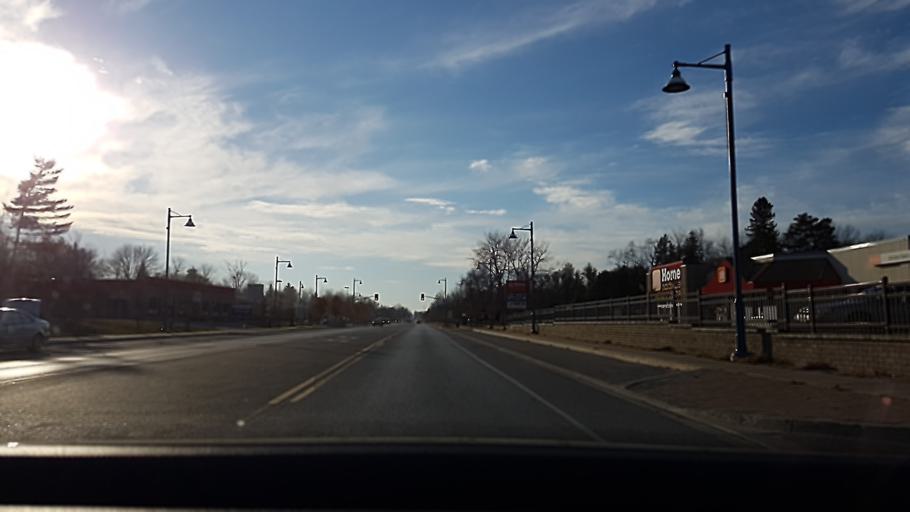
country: CA
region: Ontario
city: Keswick
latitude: 44.3164
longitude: -79.5414
